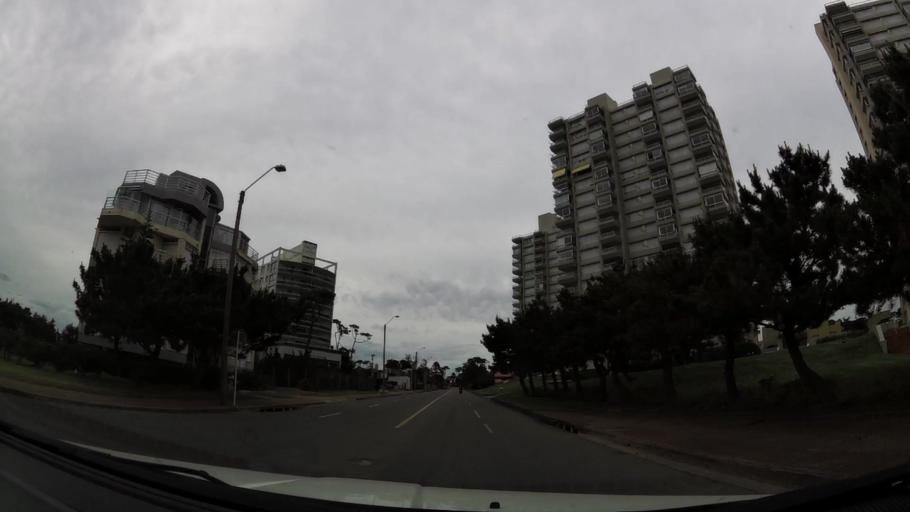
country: UY
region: Maldonado
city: Maldonado
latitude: -34.9264
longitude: -54.9630
